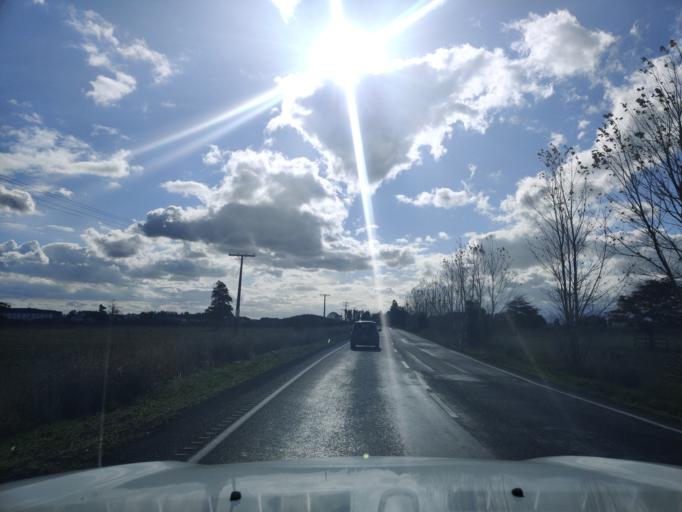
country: NZ
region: Waikato
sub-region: Hauraki District
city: Ngatea
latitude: -37.3015
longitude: 175.5586
